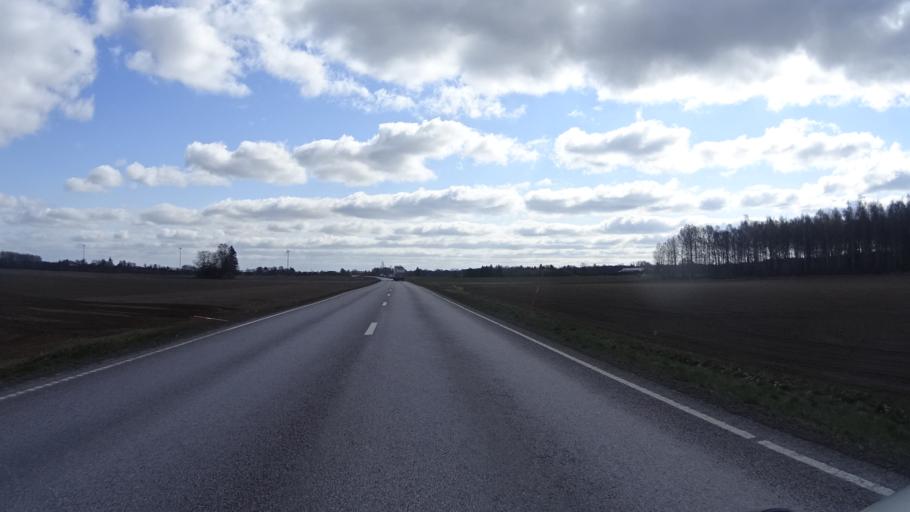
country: SE
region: OEstergoetland
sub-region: Mjolby Kommun
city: Mjolby
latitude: 58.3812
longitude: 15.1710
